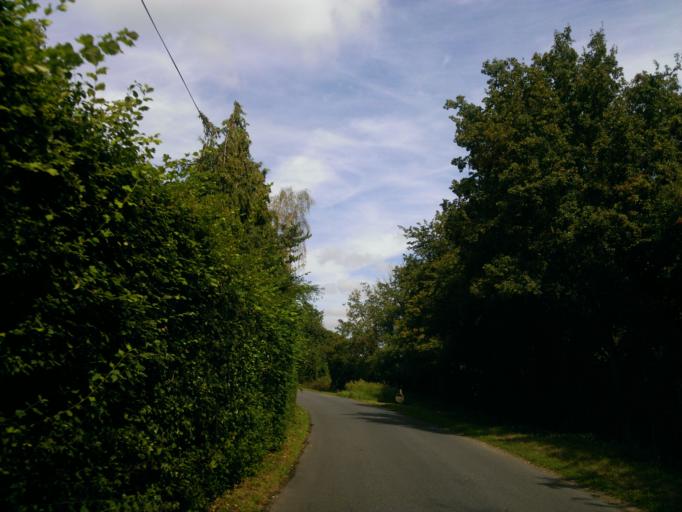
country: GB
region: England
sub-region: Essex
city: Sible Hedingham
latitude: 51.9694
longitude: 0.6223
